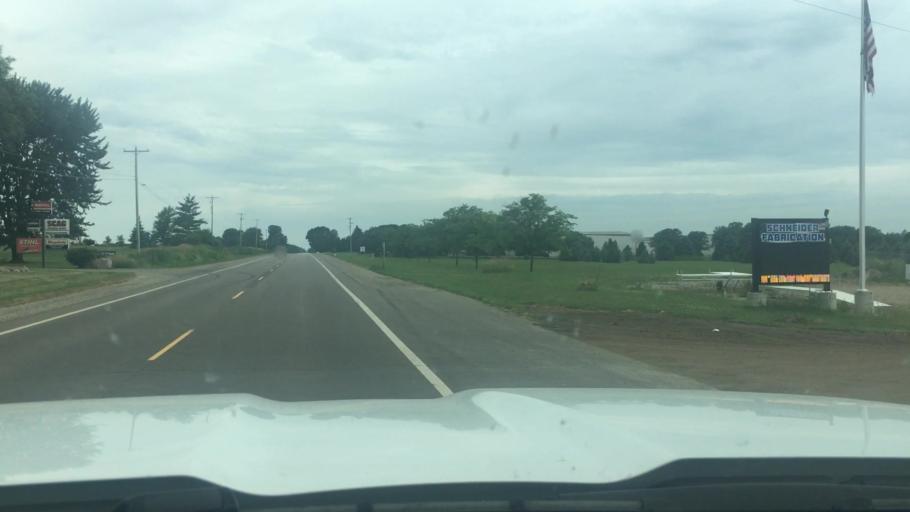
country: US
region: Michigan
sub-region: Clinton County
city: Saint Johns
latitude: 43.0015
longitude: -84.5866
